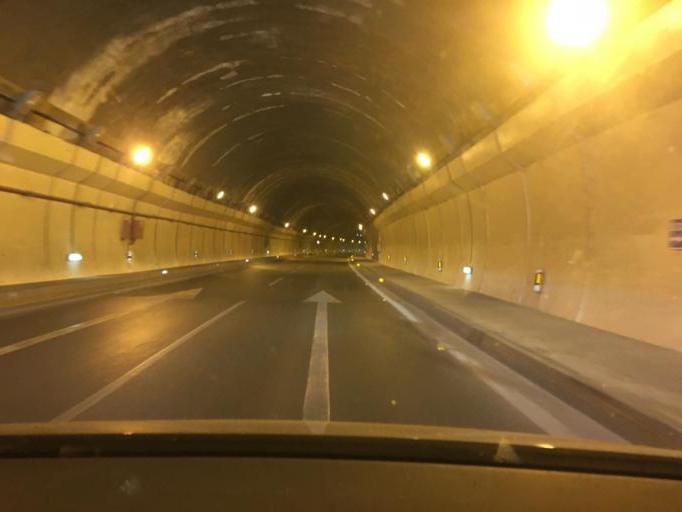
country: ES
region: Andalusia
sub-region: Provincia de Granada
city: Huetor Vega
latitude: 37.1606
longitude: -3.5726
